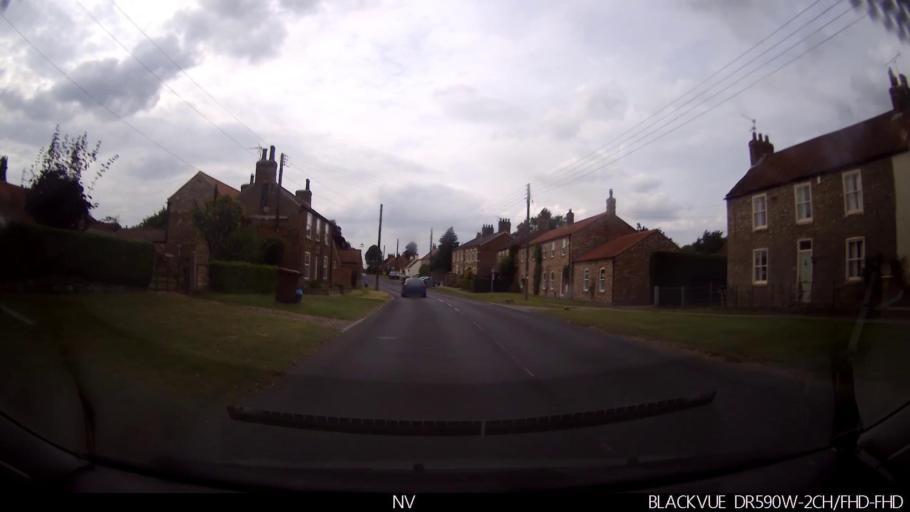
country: GB
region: England
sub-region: City of York
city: Holtby
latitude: 54.0514
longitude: -0.9621
